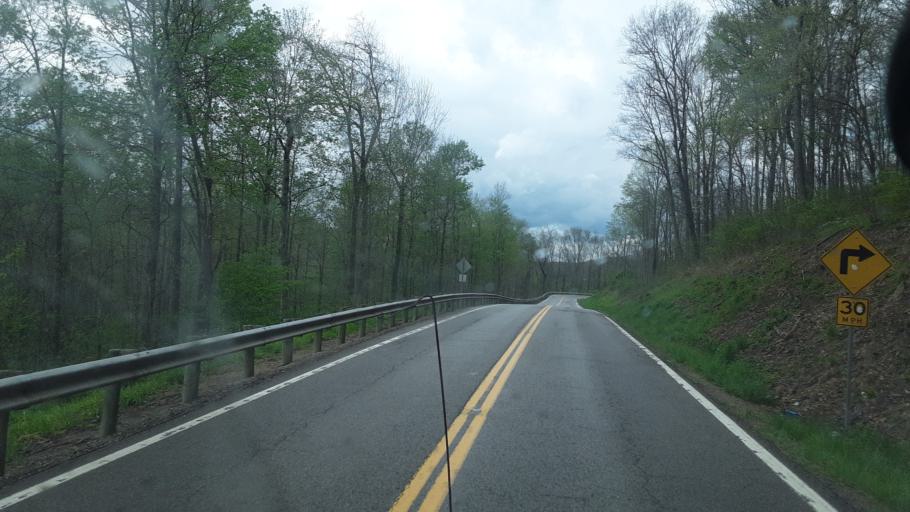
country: US
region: Ohio
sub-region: Guernsey County
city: Mantua
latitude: 40.0909
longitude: -81.7683
